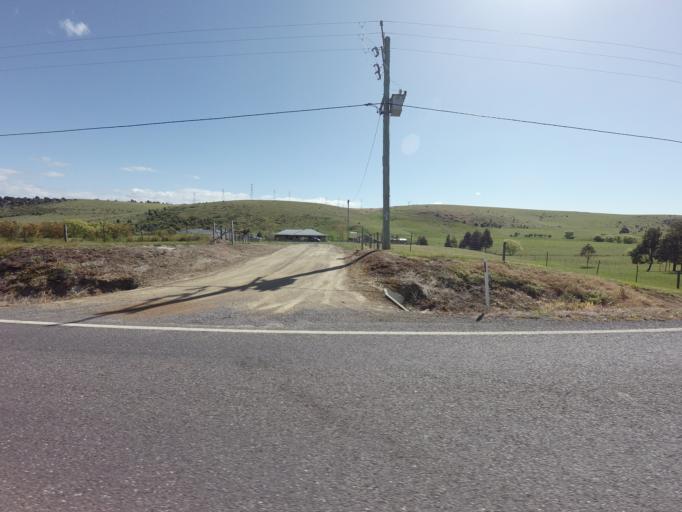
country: AU
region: Tasmania
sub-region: Derwent Valley
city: New Norfolk
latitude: -42.6597
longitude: 146.9357
